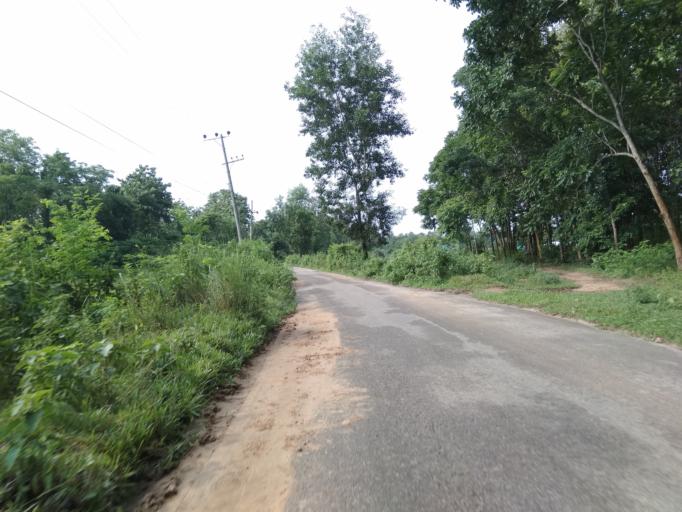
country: BD
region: Chittagong
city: Khagrachhari
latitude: 23.0277
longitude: 92.0144
